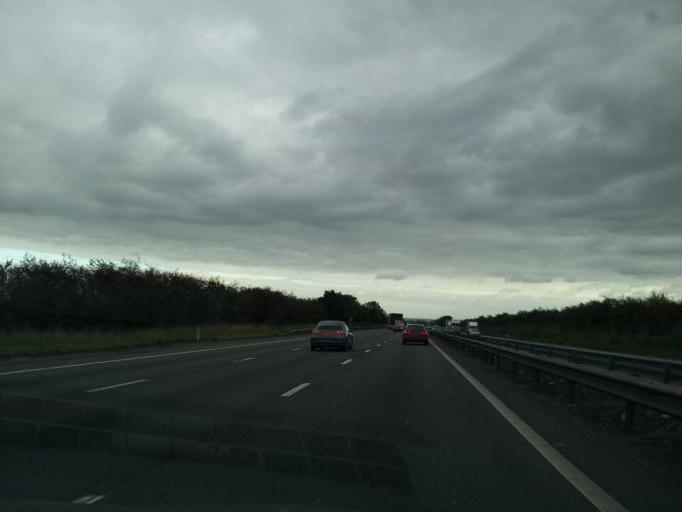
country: GB
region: England
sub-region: Milton Keynes
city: Hanslope
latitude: 52.1277
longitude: -0.8178
